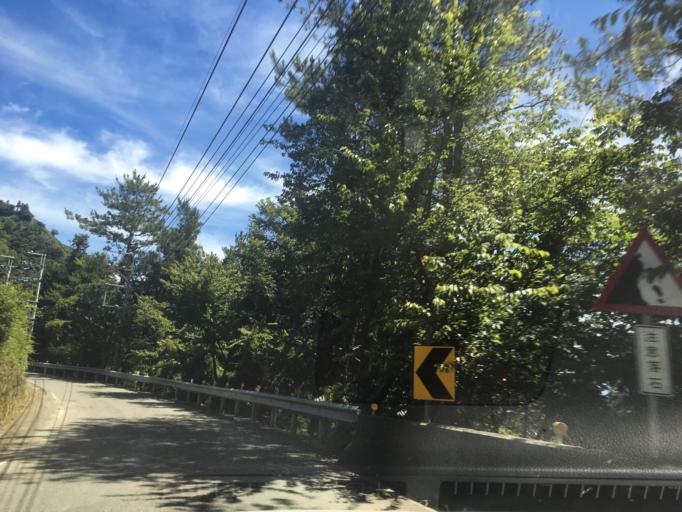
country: TW
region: Taiwan
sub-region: Nantou
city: Puli
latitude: 24.2348
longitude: 121.2553
